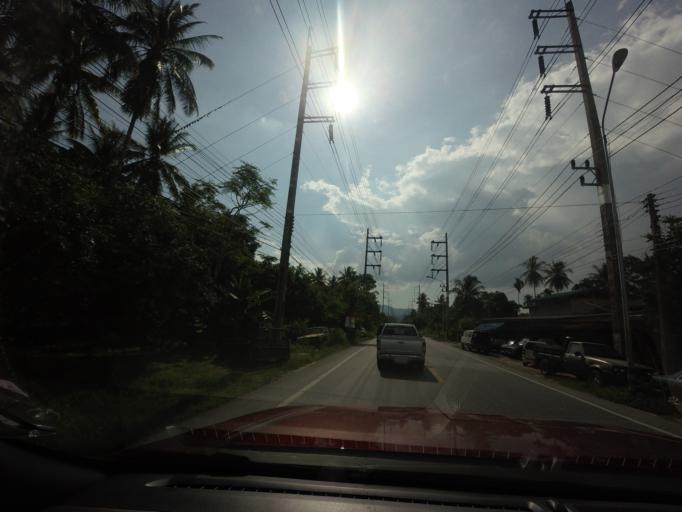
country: TH
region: Yala
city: Yala
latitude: 6.5706
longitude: 101.2043
